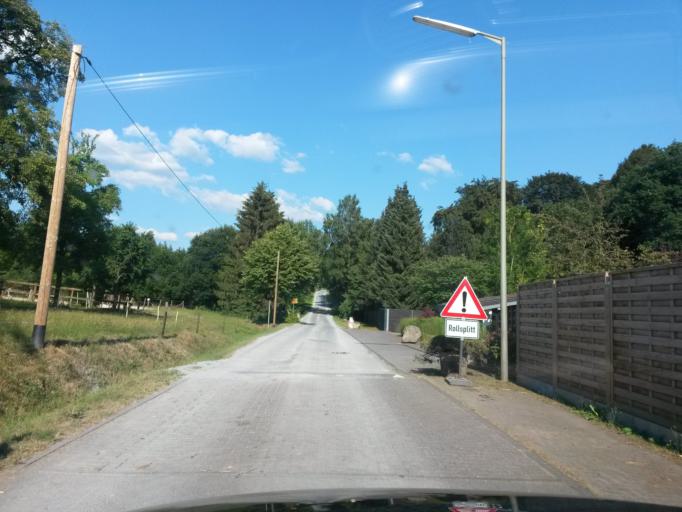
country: DE
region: North Rhine-Westphalia
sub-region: Regierungsbezirk Koln
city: Much
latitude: 50.9341
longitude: 7.4090
